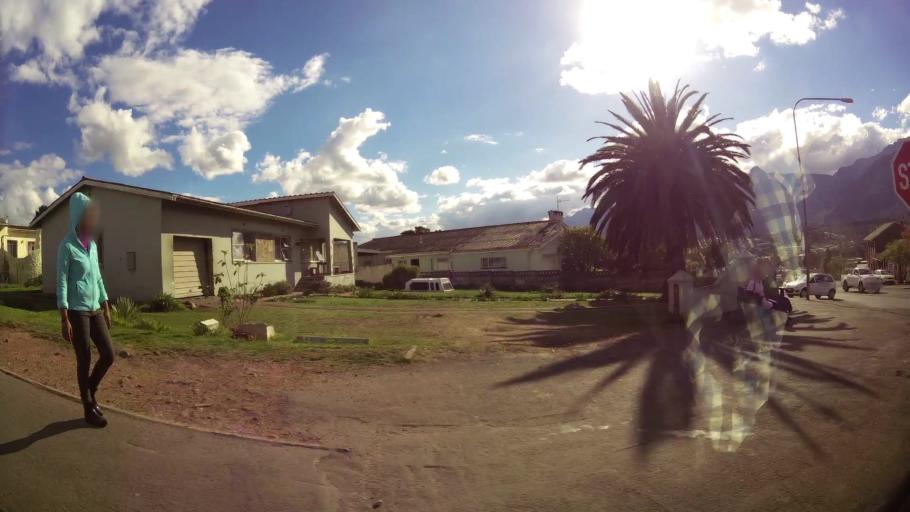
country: ZA
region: Western Cape
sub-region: Overberg District Municipality
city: Swellendam
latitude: -34.0344
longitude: 20.4441
